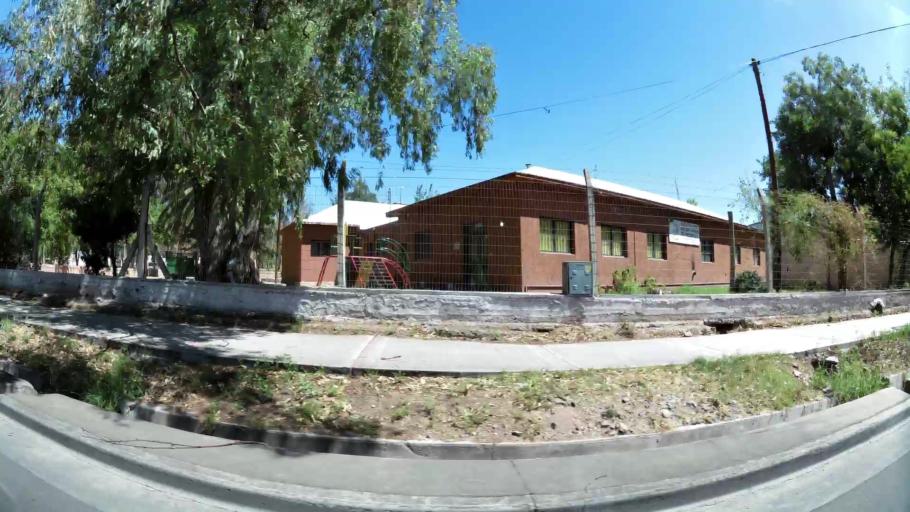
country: AR
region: Mendoza
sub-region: Departamento de Godoy Cruz
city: Godoy Cruz
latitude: -32.9157
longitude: -68.8641
